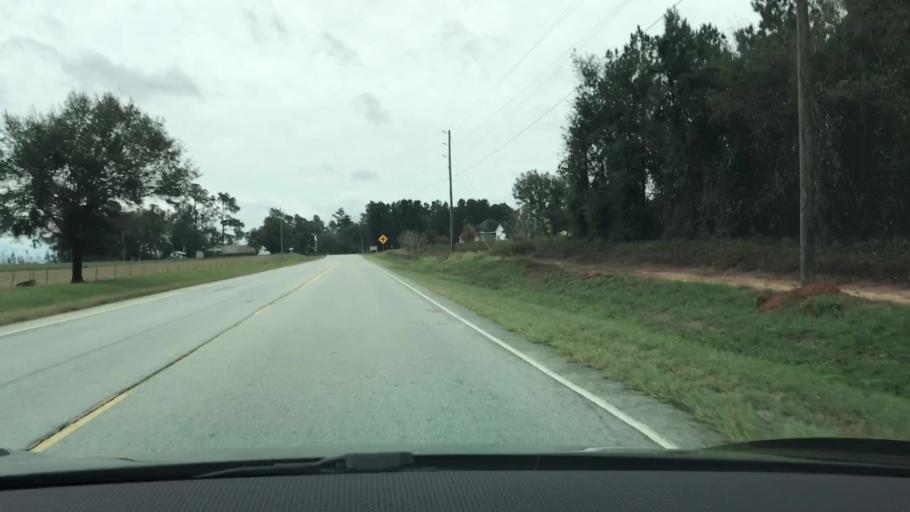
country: US
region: Georgia
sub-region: Jefferson County
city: Wrens
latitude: 33.1269
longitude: -82.4503
